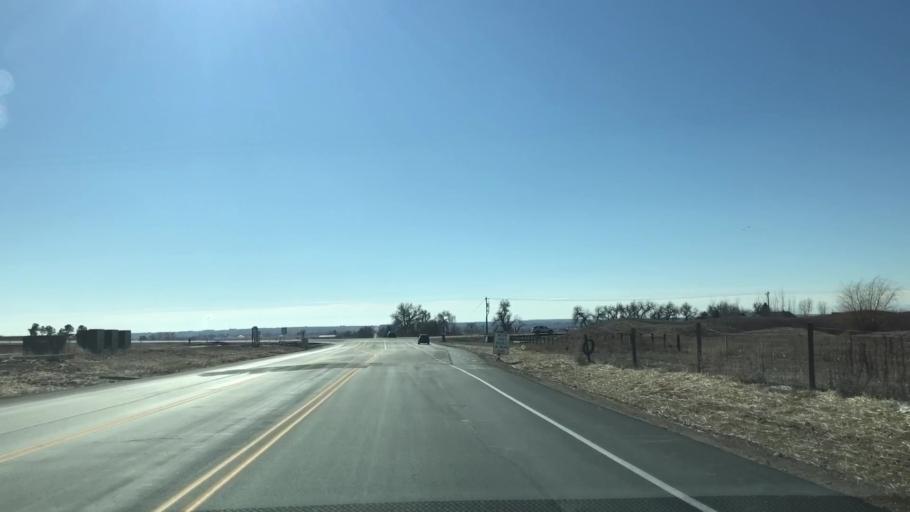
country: US
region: Colorado
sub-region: Weld County
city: Windsor
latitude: 40.5245
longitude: -104.9443
